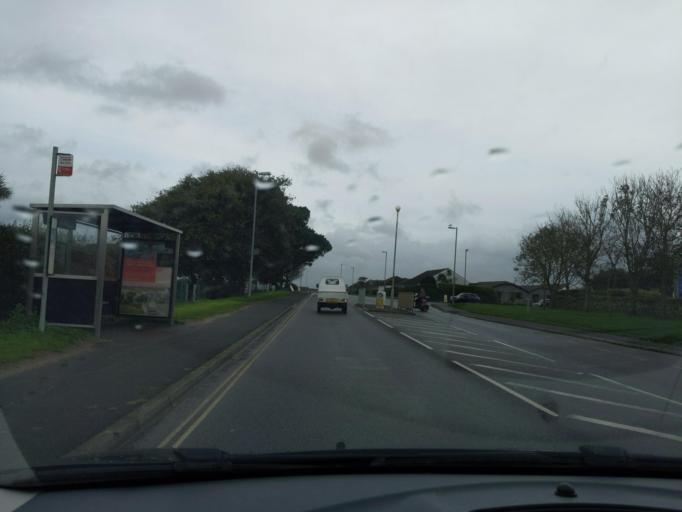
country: GB
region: England
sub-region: Cornwall
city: Padstow
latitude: 50.5357
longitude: -4.9460
